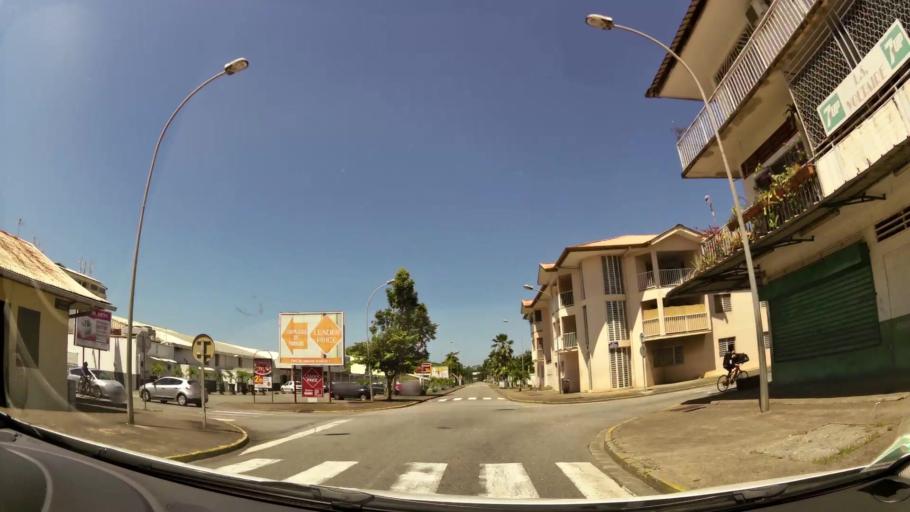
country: GF
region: Guyane
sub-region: Guyane
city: Cayenne
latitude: 4.9423
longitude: -52.3226
